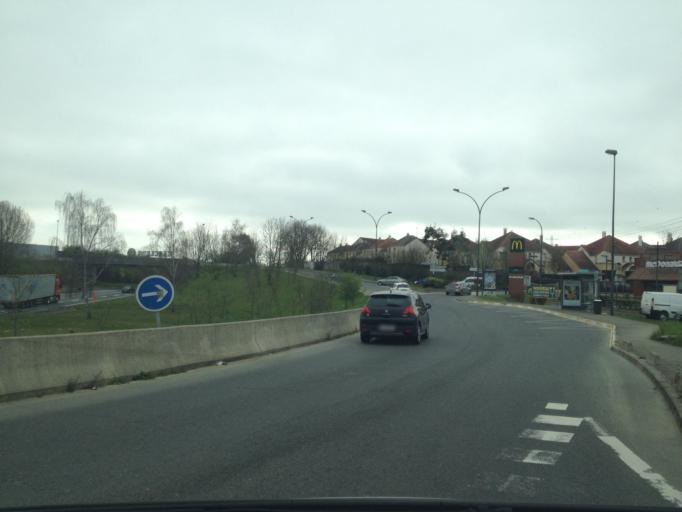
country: FR
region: Ile-de-France
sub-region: Departement de l'Essonne
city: Palaiseau
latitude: 48.7306
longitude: 2.2408
